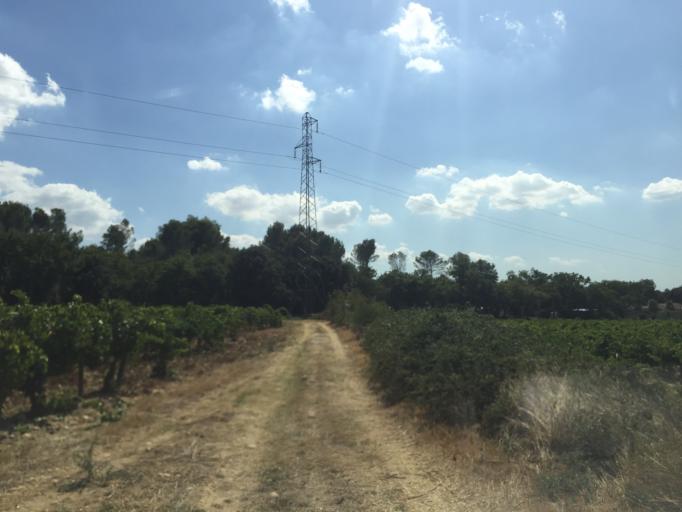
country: FR
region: Provence-Alpes-Cote d'Azur
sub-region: Departement du Vaucluse
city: Bedarrides
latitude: 44.0229
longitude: 4.8928
